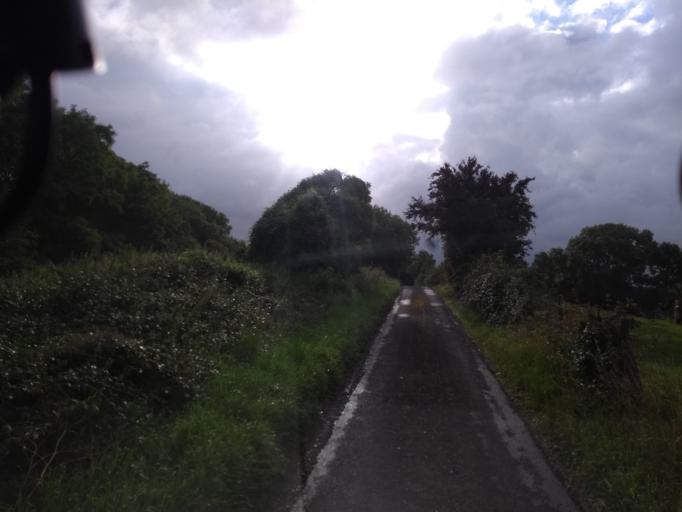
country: GB
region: England
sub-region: Somerset
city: Castle Cary
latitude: 51.0275
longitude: -2.5833
